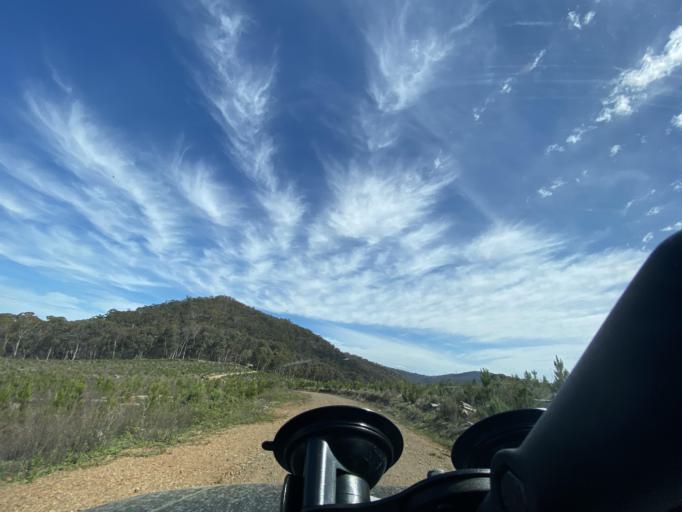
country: AU
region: Victoria
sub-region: Mansfield
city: Mansfield
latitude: -36.8303
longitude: 146.1016
